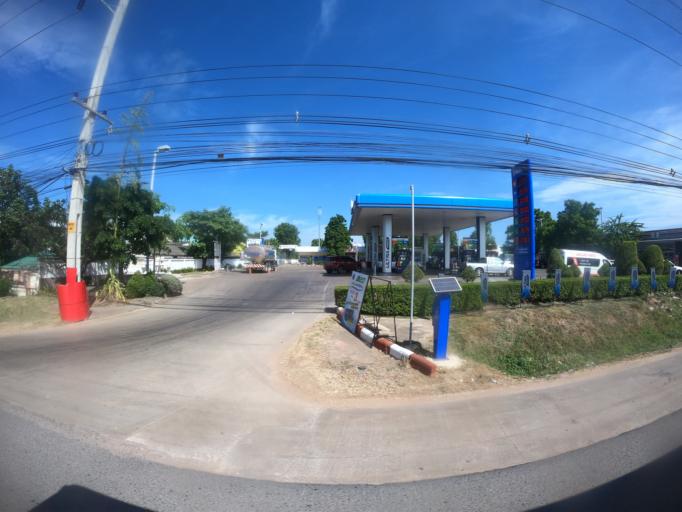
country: TH
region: Khon Kaen
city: Khon Kaen
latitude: 16.4379
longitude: 102.9357
